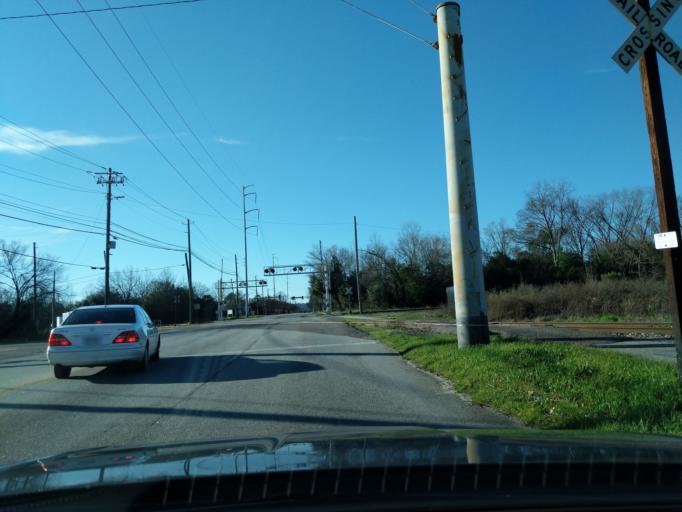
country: US
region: Georgia
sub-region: Richmond County
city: Augusta
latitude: 33.4614
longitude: -81.9675
